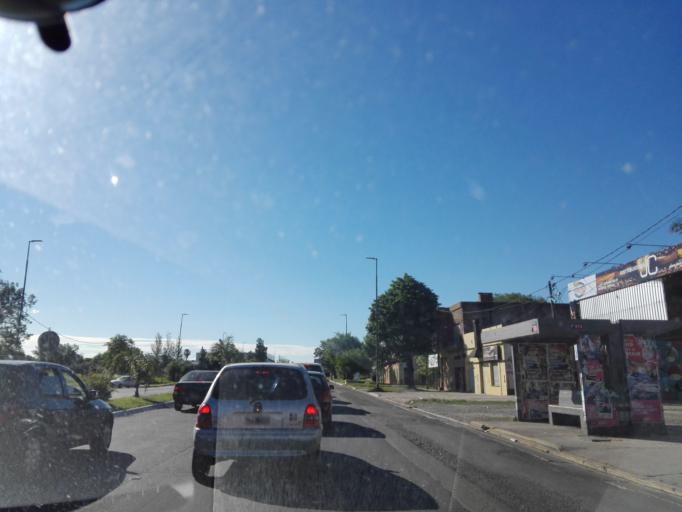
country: AR
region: Buenos Aires
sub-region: Partido de La Plata
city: La Plata
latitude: -34.8907
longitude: -57.9959
